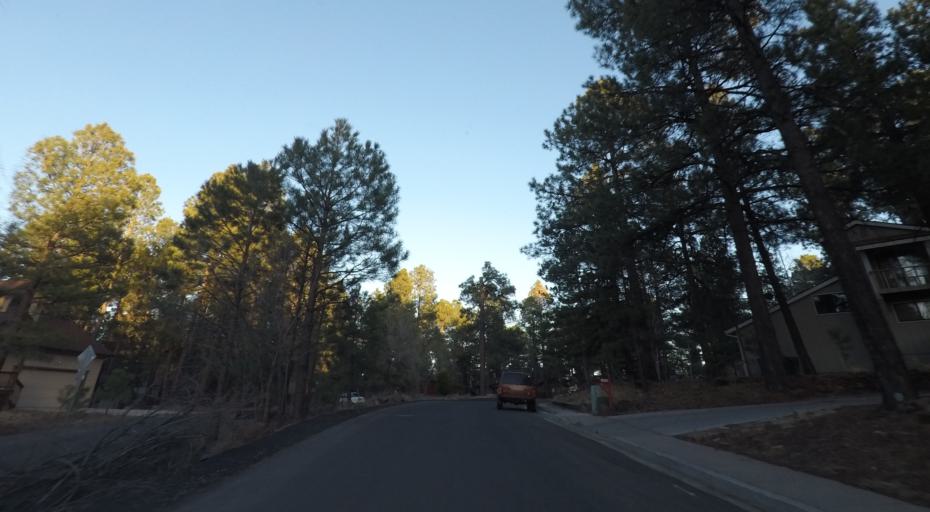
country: US
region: Arizona
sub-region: Coconino County
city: Flagstaff
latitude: 35.1748
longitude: -111.6769
